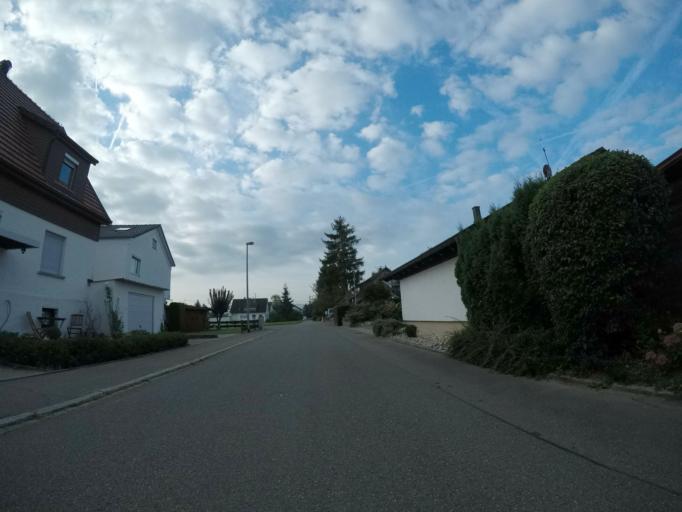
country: DE
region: Baden-Wuerttemberg
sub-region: Tuebingen Region
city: Sickenhausen
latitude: 48.5199
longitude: 9.1738
